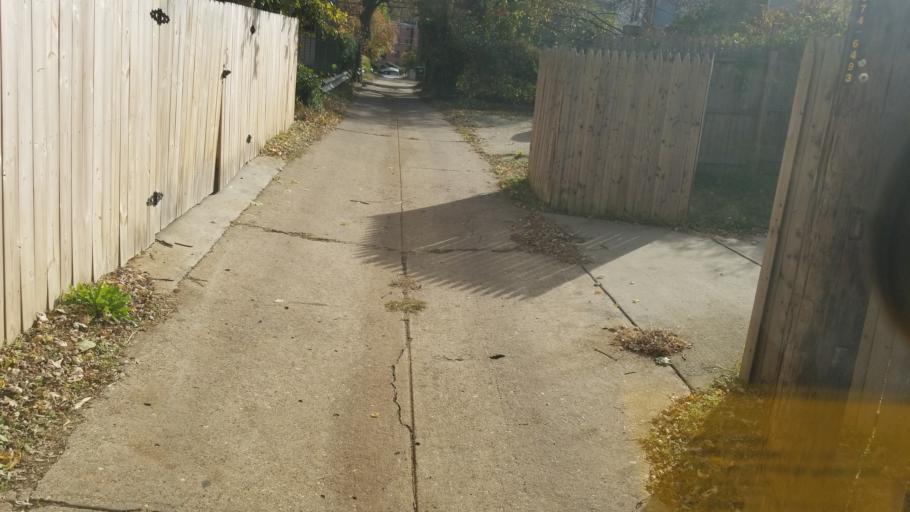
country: US
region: Maryland
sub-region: Prince George's County
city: Hillcrest Heights
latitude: 38.8630
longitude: -76.9869
